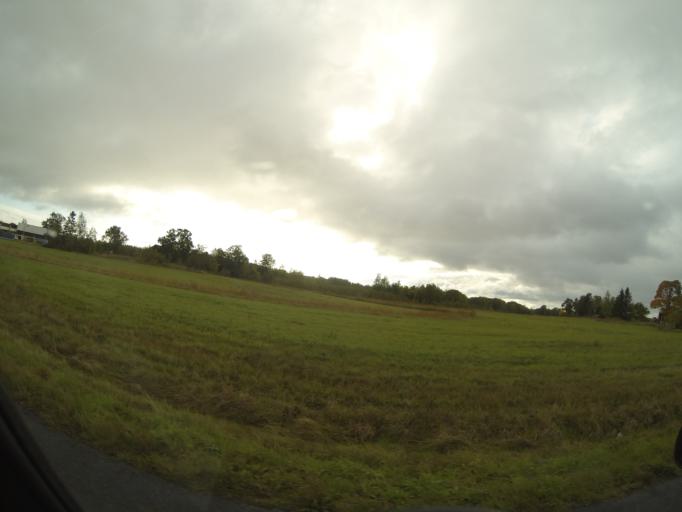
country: SE
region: Soedermanland
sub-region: Eskilstuna Kommun
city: Kvicksund
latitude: 59.3206
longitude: 16.3099
